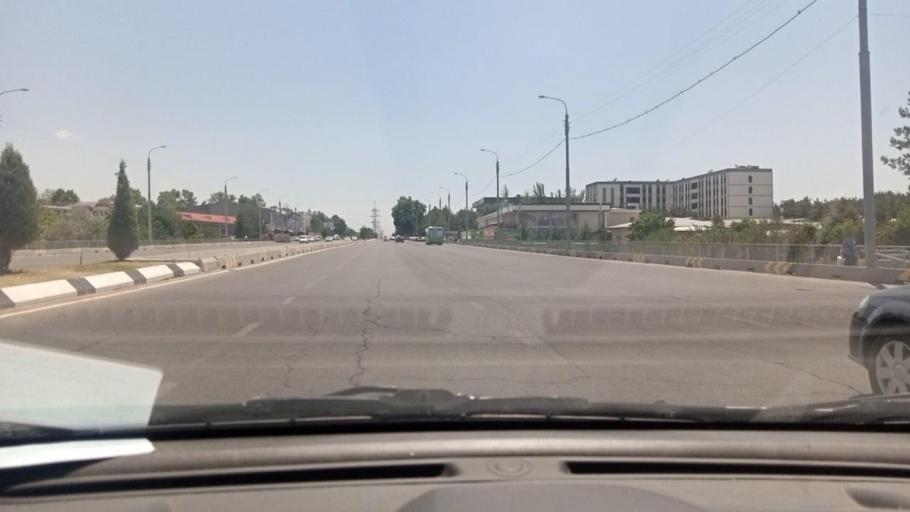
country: UZ
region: Toshkent Shahri
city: Tashkent
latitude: 41.3039
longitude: 69.1937
